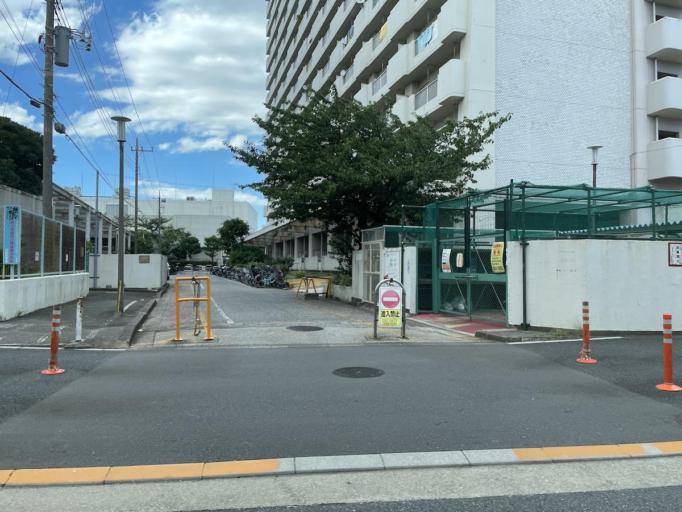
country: JP
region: Tokyo
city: Urayasu
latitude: 35.7101
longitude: 139.8354
